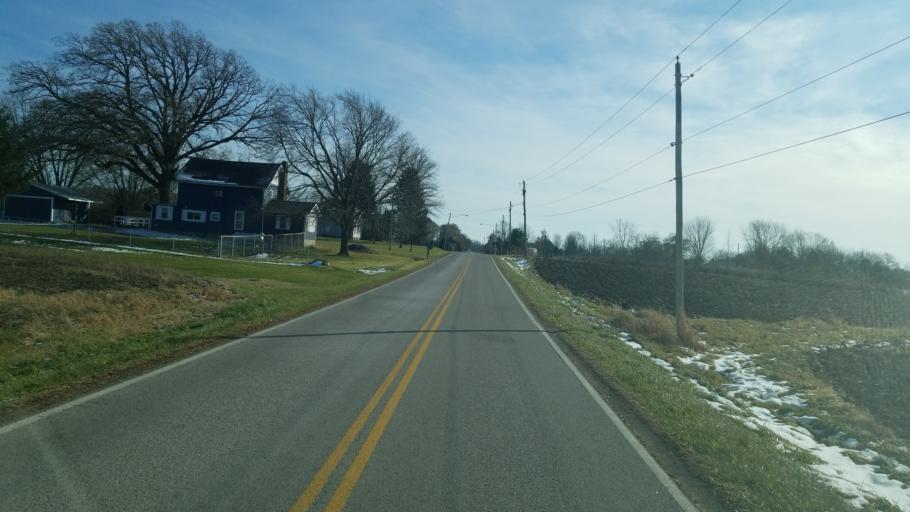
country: US
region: Ohio
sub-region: Lorain County
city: Camden
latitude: 41.1865
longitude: -82.3548
